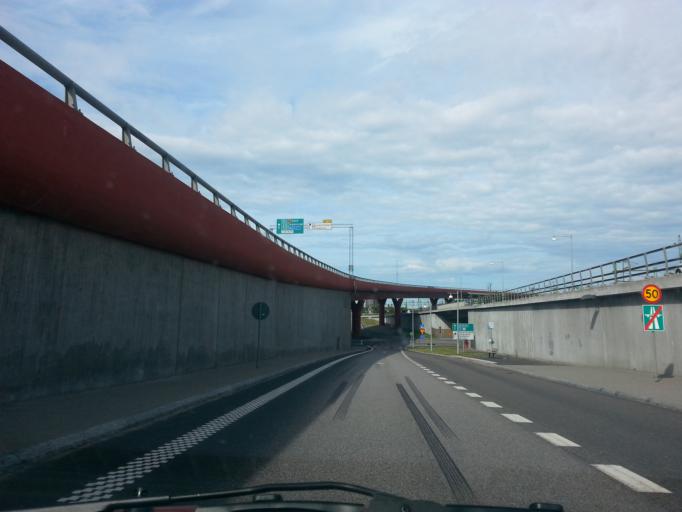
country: SE
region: Vaestra Goetaland
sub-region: Goteborg
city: Goeteborg
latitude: 57.7238
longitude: 12.0109
